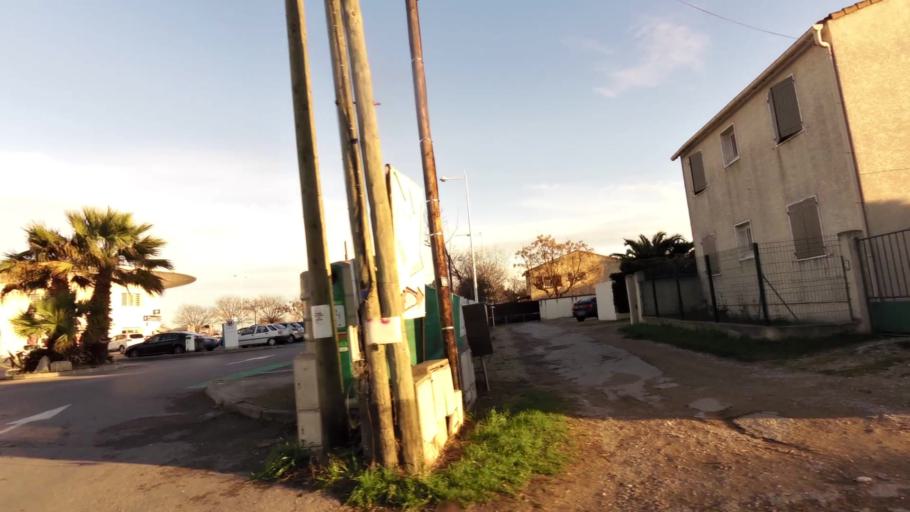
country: FR
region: Languedoc-Roussillon
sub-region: Departement du Gard
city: Aigues-Mortes
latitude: 43.5760
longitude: 4.1978
